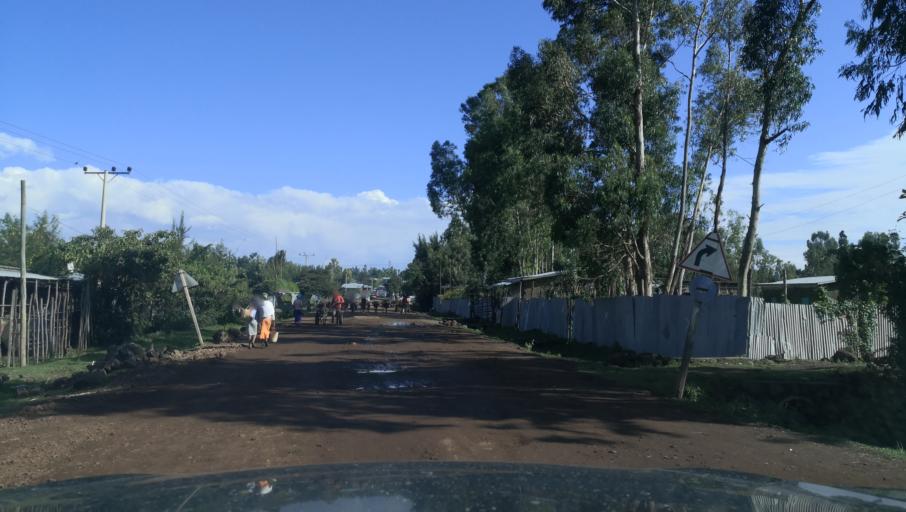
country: ET
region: Oromiya
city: Tulu Bolo
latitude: 8.6552
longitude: 38.2183
